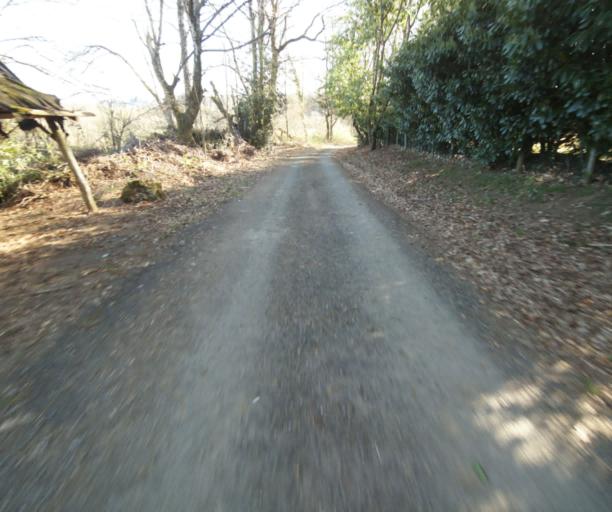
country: FR
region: Limousin
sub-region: Departement de la Correze
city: Seilhac
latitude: 45.3864
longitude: 1.7065
